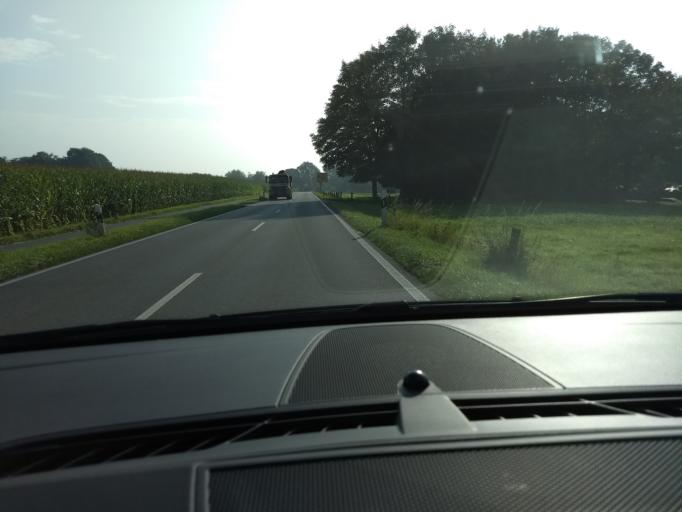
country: DE
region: North Rhine-Westphalia
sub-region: Regierungsbezirk Munster
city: Heiden
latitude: 51.8329
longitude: 6.9238
